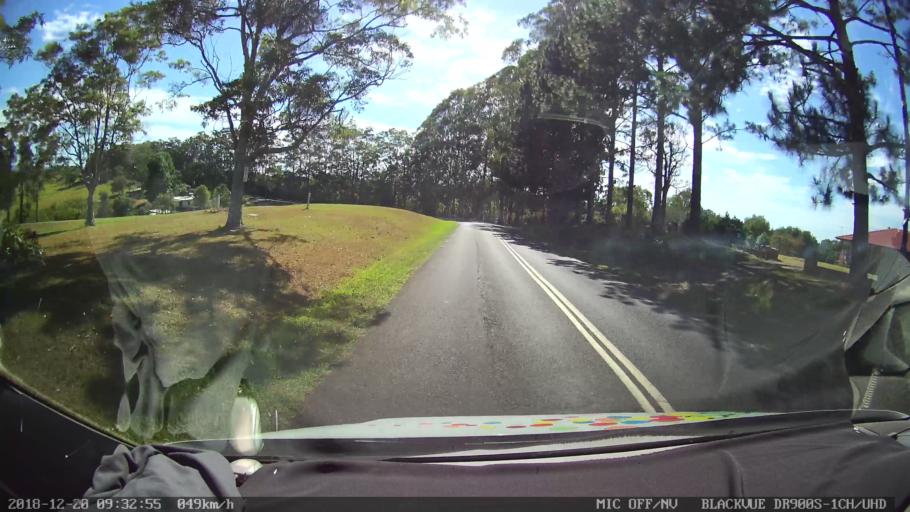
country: AU
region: New South Wales
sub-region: Lismore Municipality
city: Lismore
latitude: -28.6982
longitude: 153.3055
